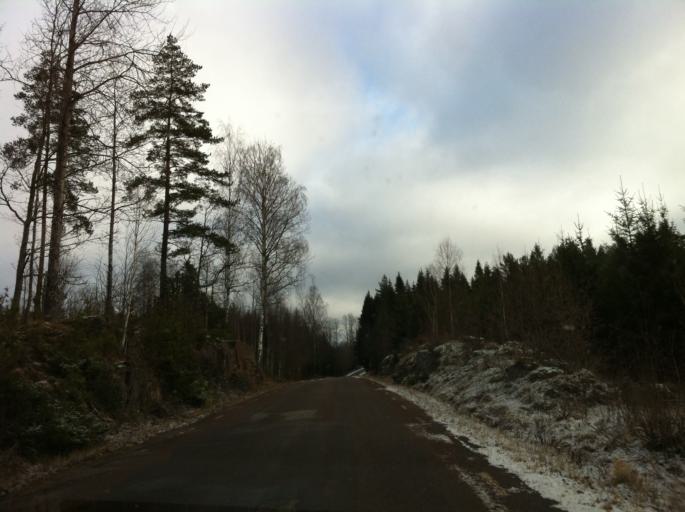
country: SE
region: Joenkoeping
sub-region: Eksjo Kommun
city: Mariannelund
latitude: 57.6132
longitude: 15.6772
